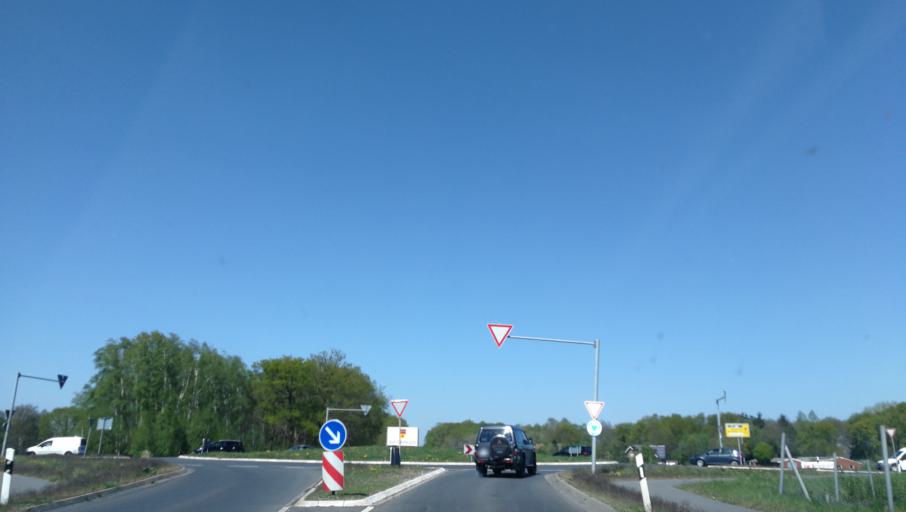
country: DE
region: North Rhine-Westphalia
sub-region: Regierungsbezirk Munster
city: Wettringen
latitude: 52.1978
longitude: 7.3238
